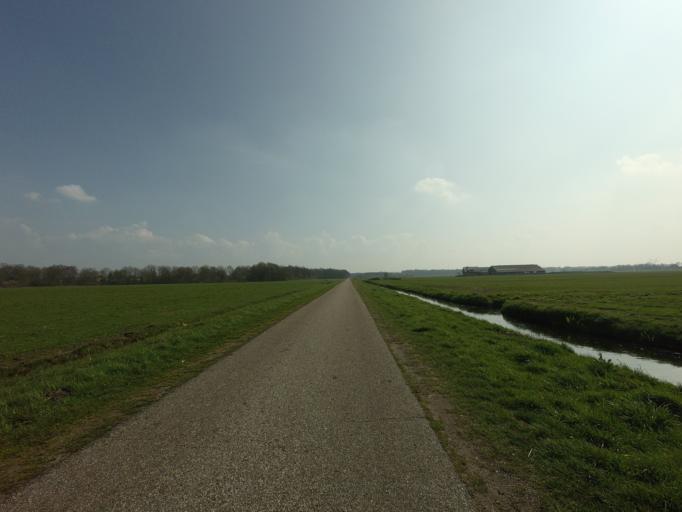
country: NL
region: North Holland
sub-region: Gemeente Bussum
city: Bussum
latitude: 52.2718
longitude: 5.1269
